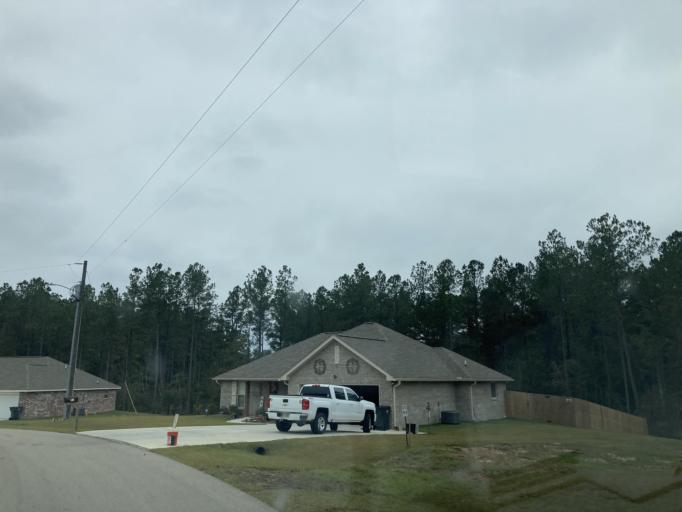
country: US
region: Mississippi
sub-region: Lamar County
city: Purvis
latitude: 31.1768
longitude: -89.4219
